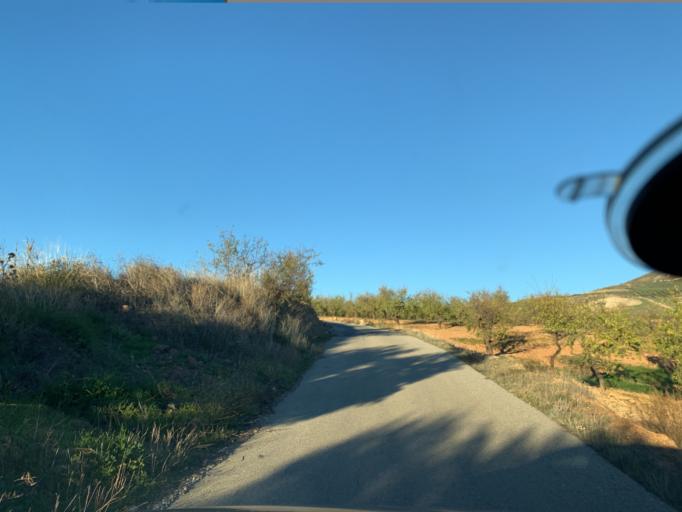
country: ES
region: Andalusia
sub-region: Provincia de Granada
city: Dilar
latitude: 37.0717
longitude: -3.5810
